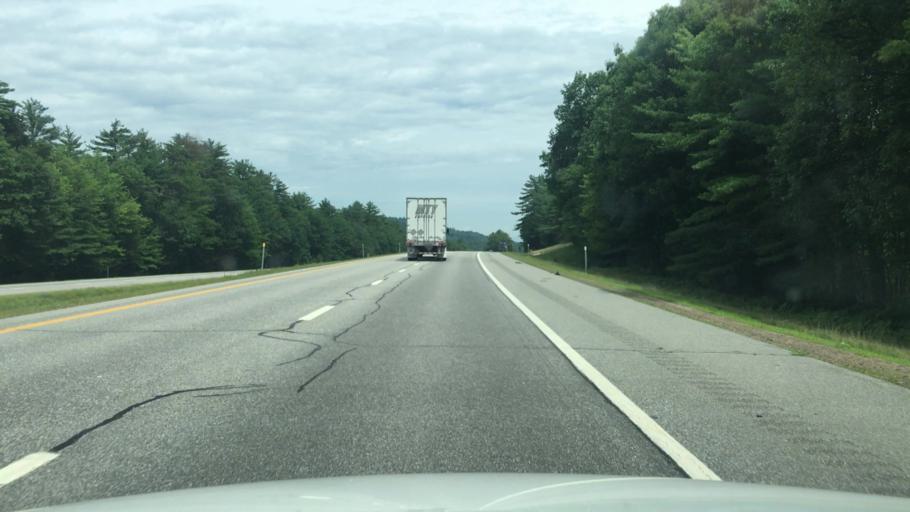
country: US
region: New Hampshire
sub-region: Grafton County
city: Ashland
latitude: 43.6573
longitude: -71.6489
